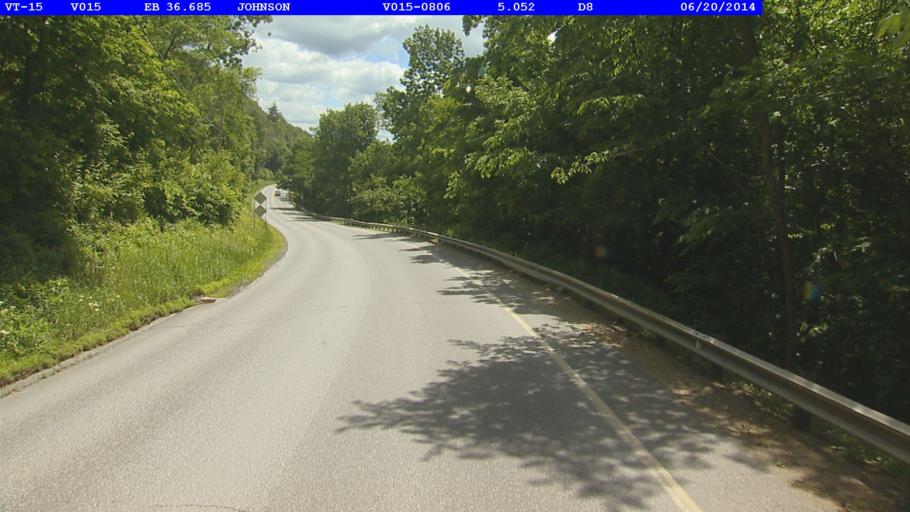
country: US
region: Vermont
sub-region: Lamoille County
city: Johnson
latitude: 44.6237
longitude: -72.6756
